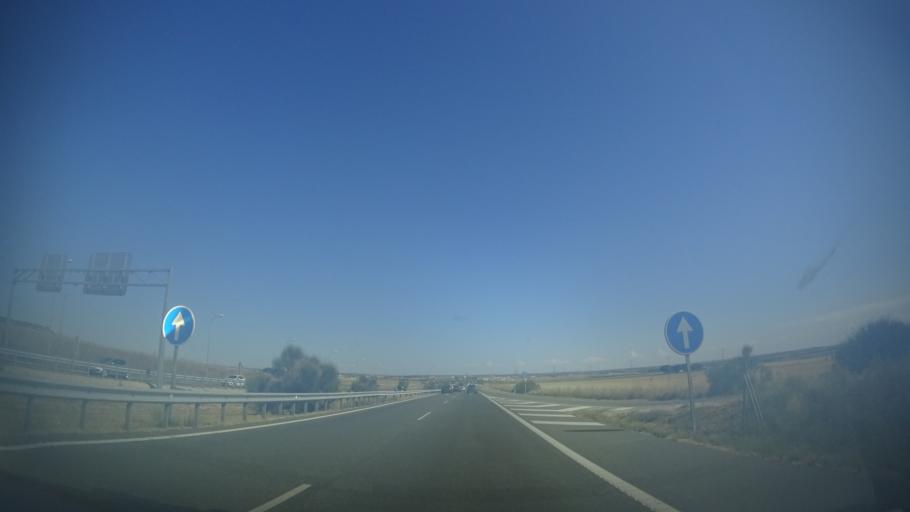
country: ES
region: Castille and Leon
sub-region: Provincia de Valladolid
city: Bercero
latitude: 41.5239
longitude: -5.0420
